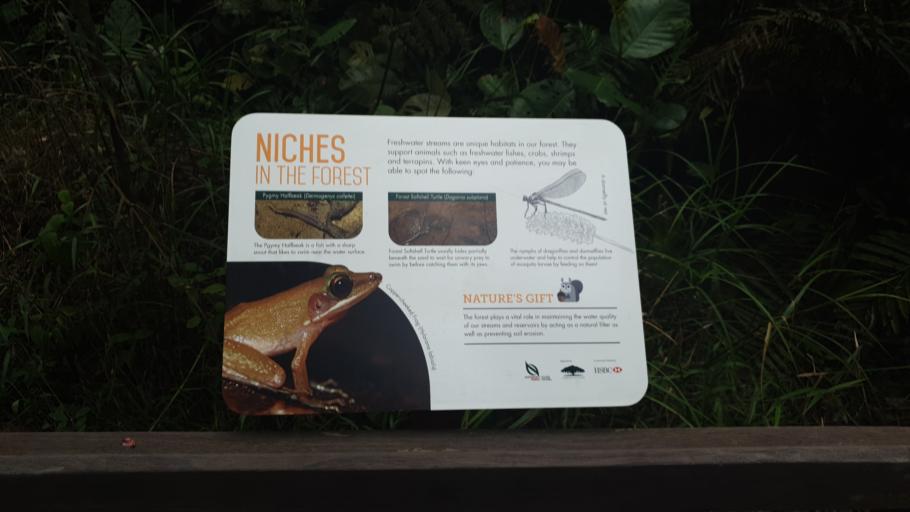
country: SG
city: Singapore
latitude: 1.3551
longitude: 103.8077
